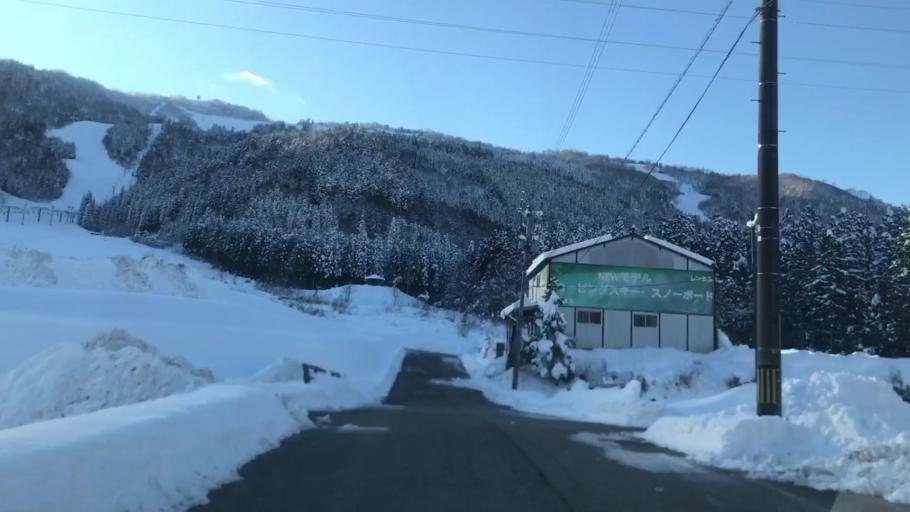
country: JP
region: Toyama
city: Kamiichi
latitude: 36.5778
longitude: 137.4256
